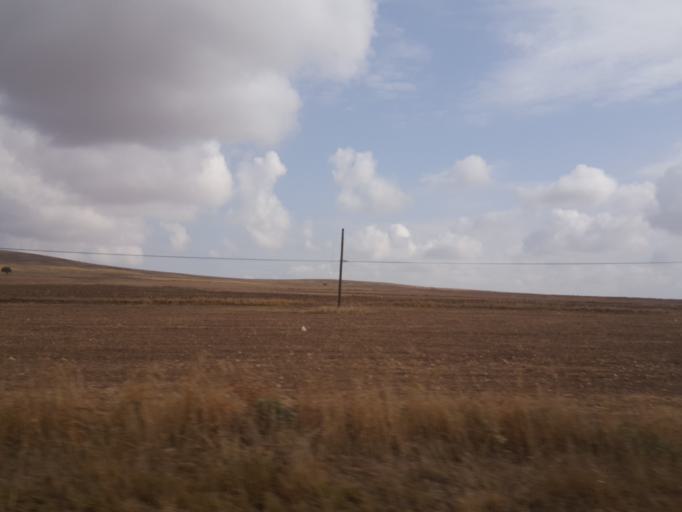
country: TR
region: Kirikkale
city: Keskin
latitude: 39.6240
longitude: 33.6118
